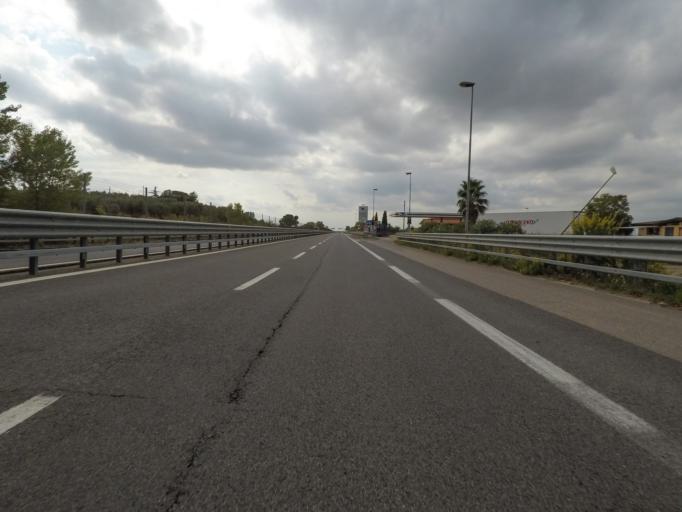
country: IT
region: Tuscany
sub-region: Provincia di Grosseto
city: Bagno Roselle
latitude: 42.8286
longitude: 11.1395
